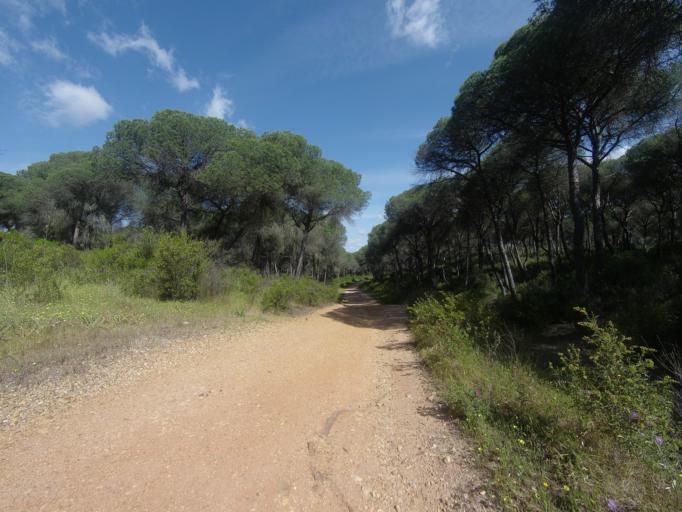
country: ES
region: Andalusia
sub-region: Provincia de Huelva
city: Aljaraque
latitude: 37.2335
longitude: -7.0498
